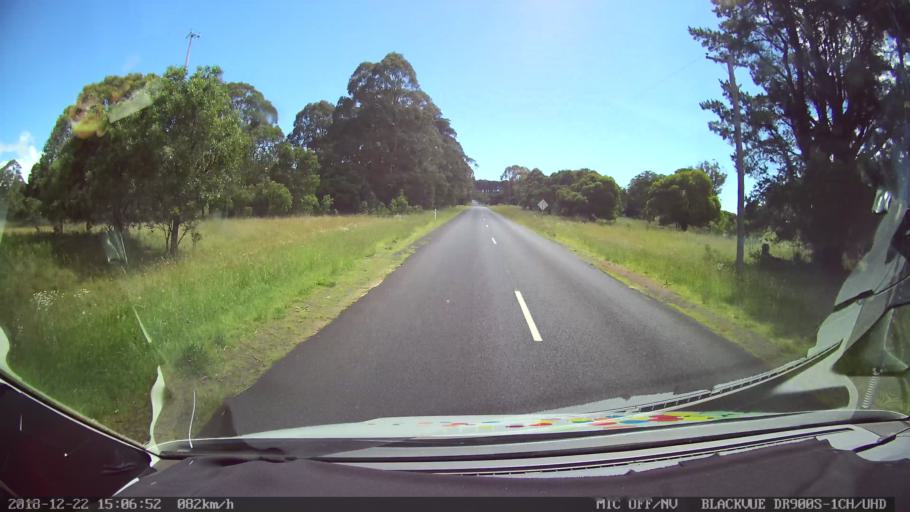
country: AU
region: New South Wales
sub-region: Bellingen
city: Dorrigo
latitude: -30.2962
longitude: 152.4220
